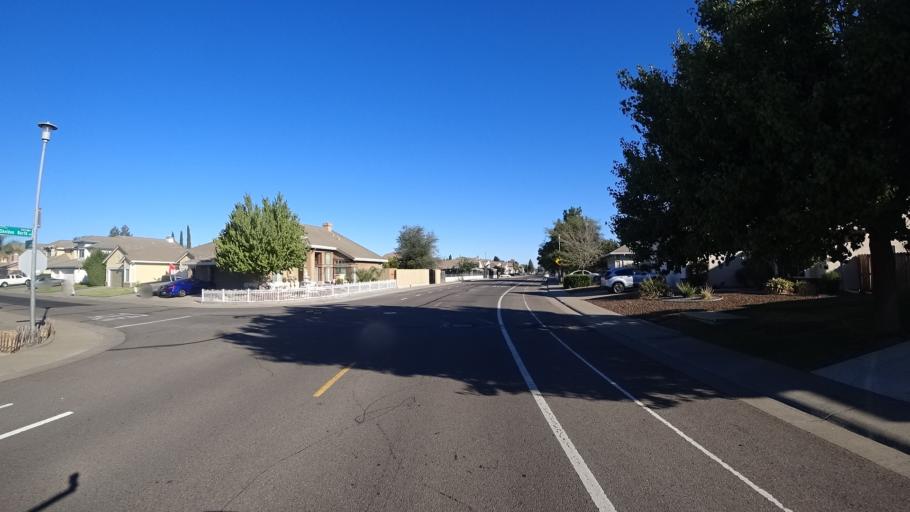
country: US
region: California
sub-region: Sacramento County
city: Vineyard
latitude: 38.4482
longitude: -121.3853
